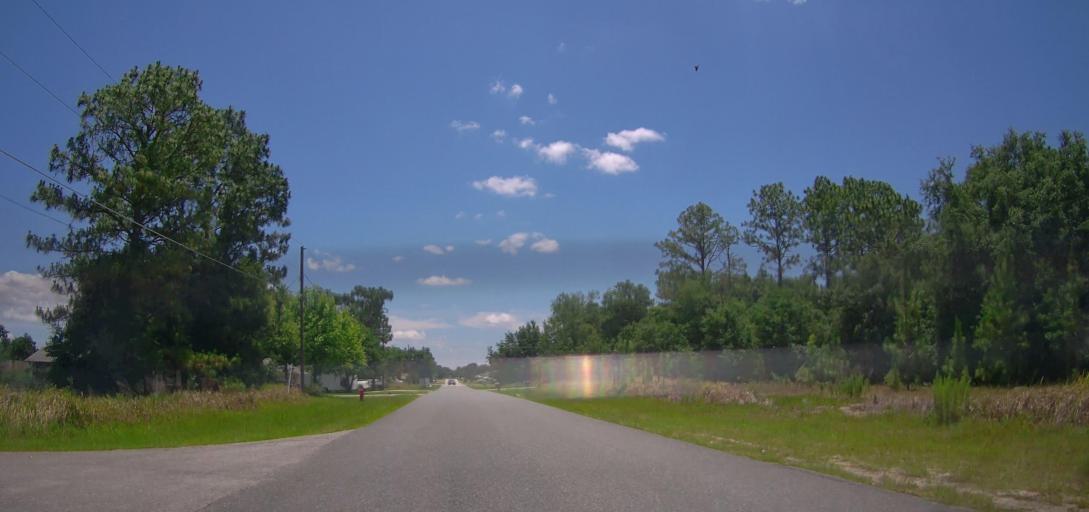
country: US
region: Florida
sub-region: Marion County
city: Silver Springs Shores
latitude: 29.1270
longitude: -82.0417
